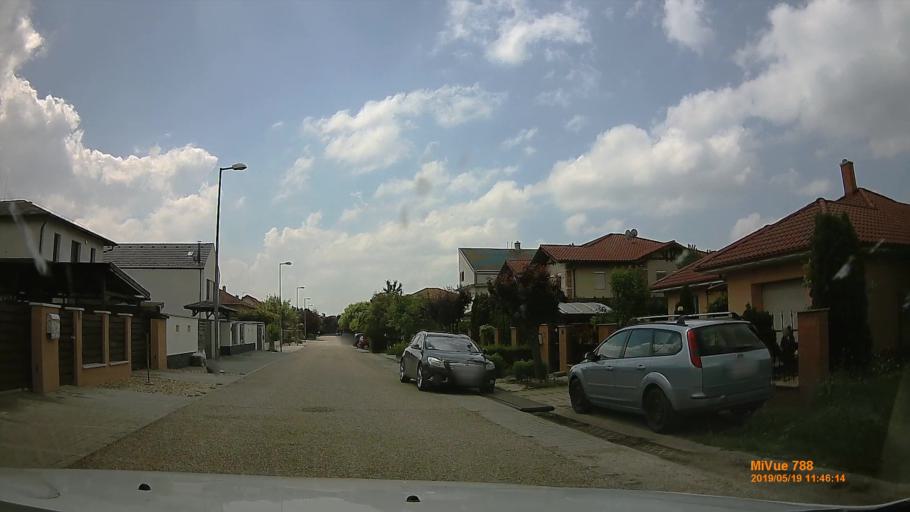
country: HU
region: Budapest
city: Budapest XVII. keruelet
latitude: 47.4728
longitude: 19.2261
